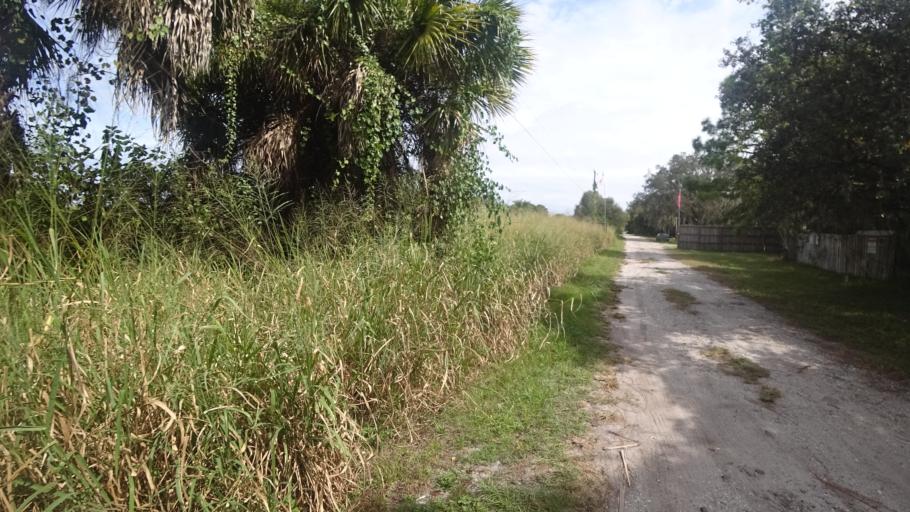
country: US
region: Florida
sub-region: Sarasota County
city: North Sarasota
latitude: 27.3870
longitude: -82.5164
